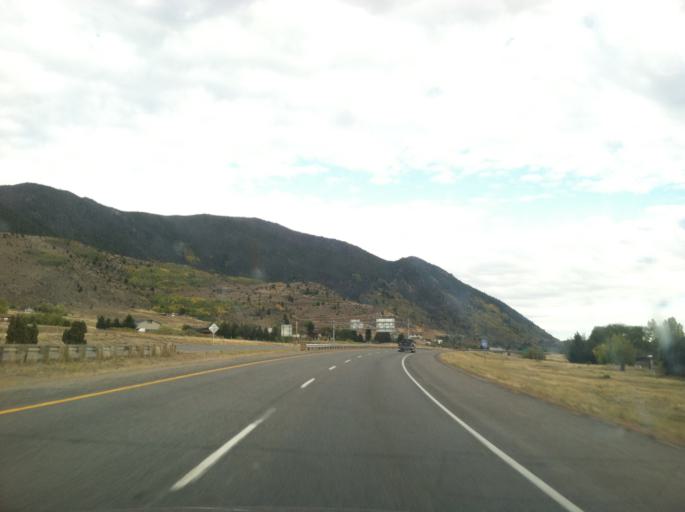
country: US
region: Montana
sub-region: Silver Bow County
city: Butte
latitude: 45.9795
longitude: -112.4797
